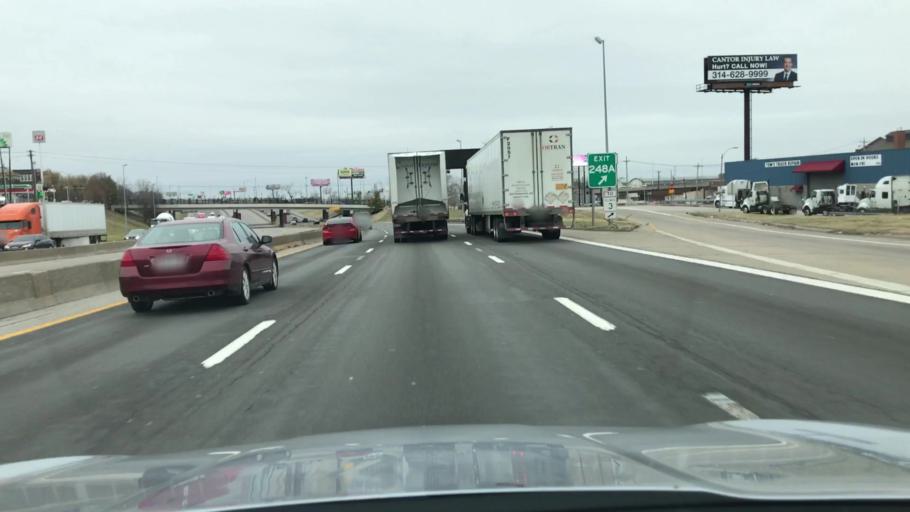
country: US
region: Illinois
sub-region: Madison County
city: Venice
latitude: 38.6595
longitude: -90.1962
